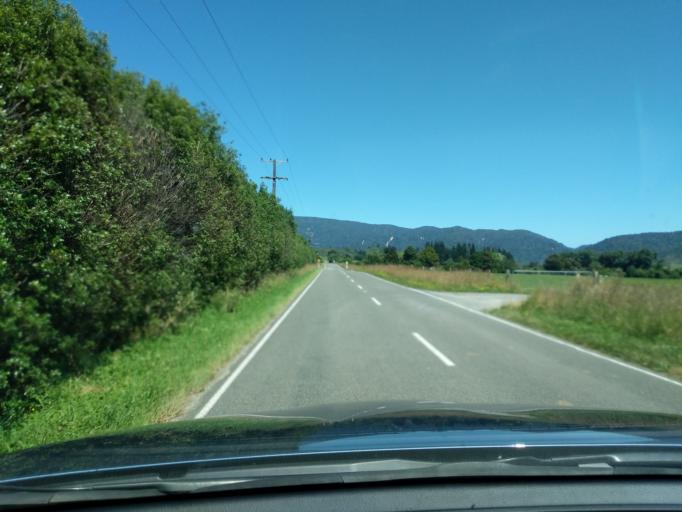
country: NZ
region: Tasman
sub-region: Tasman District
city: Takaka
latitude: -40.7291
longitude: 172.6330
